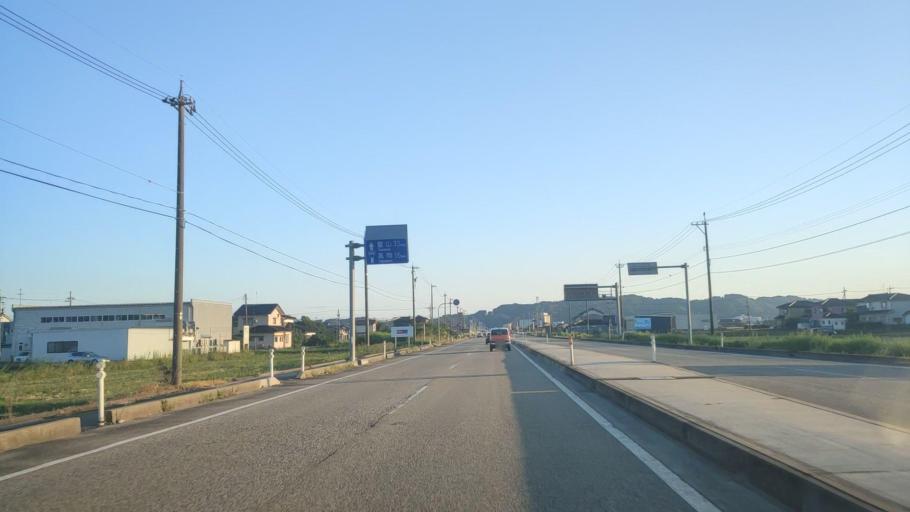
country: JP
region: Toyama
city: Himi
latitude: 36.8737
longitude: 136.9752
